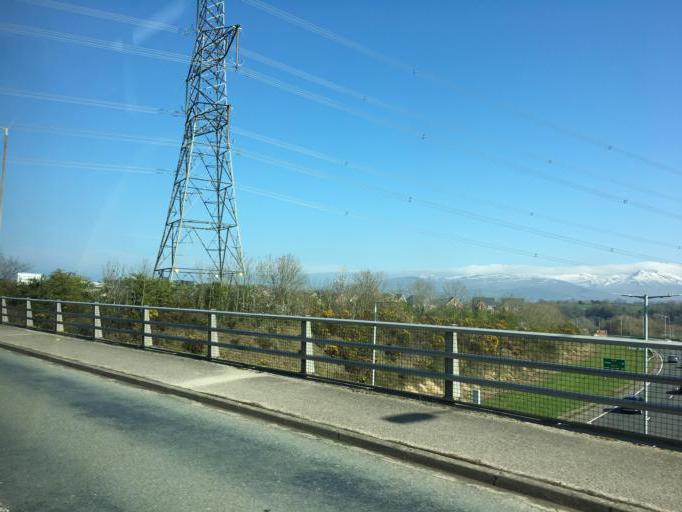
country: GB
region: Wales
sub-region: Anglesey
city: Menai Bridge
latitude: 53.2047
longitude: -4.1729
